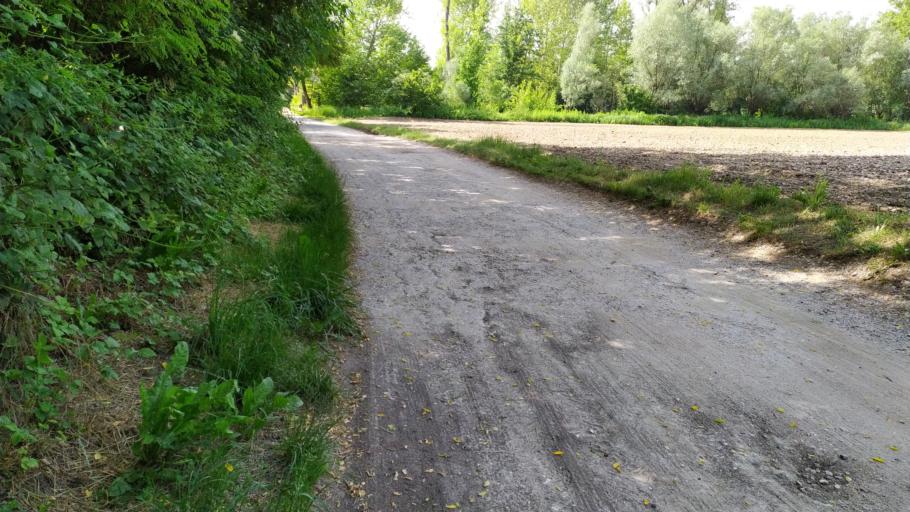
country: IT
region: Veneto
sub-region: Provincia di Treviso
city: Sernaglia della Battaglia
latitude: 45.8603
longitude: 12.1414
